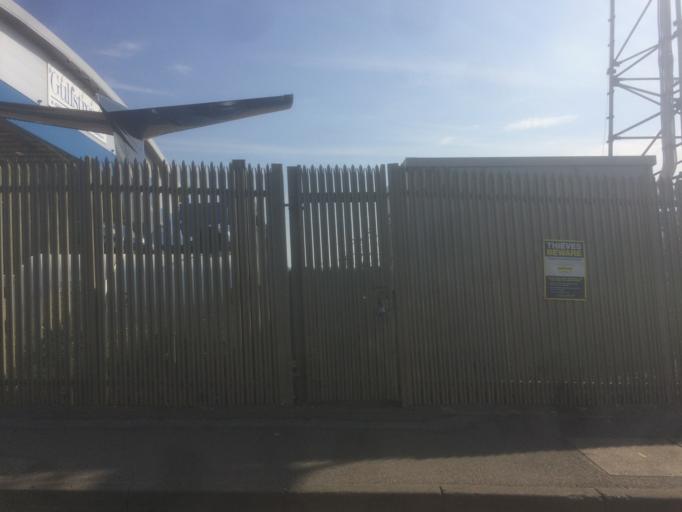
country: GB
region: England
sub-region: Luton
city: Luton
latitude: 51.8782
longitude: -0.3830
